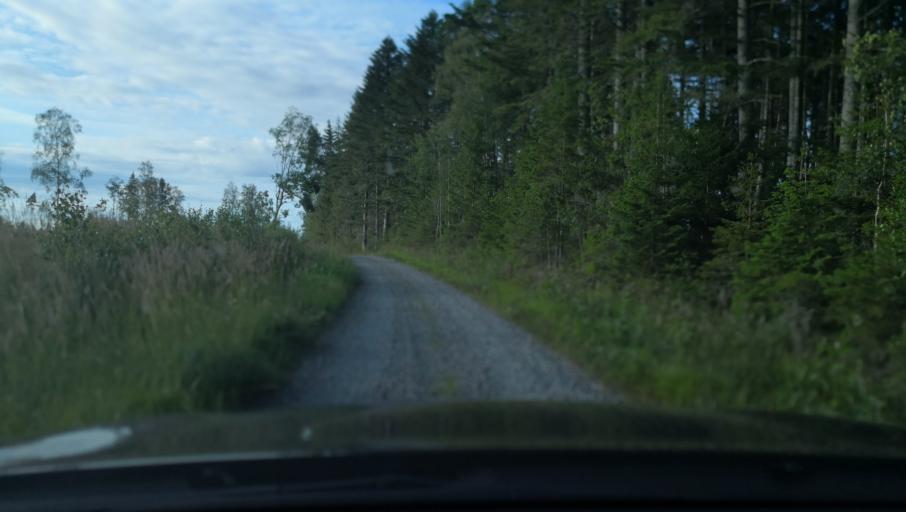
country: SE
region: Uppsala
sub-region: Osthammars Kommun
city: Osterbybruk
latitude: 60.0336
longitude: 17.9194
